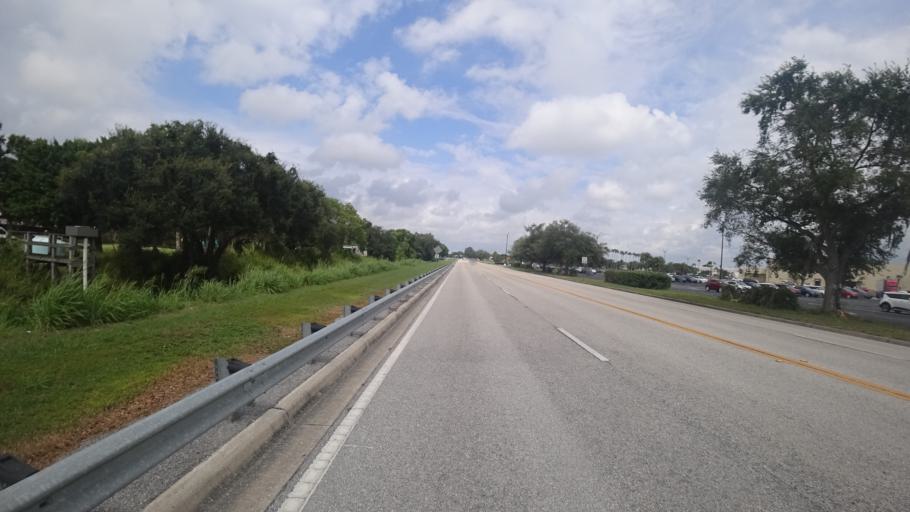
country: US
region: Florida
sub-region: Manatee County
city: South Bradenton
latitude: 27.4655
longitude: -82.5701
